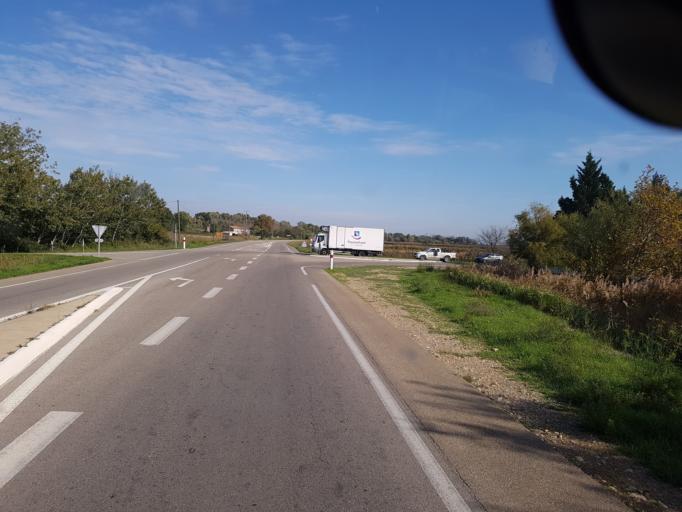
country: FR
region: Languedoc-Roussillon
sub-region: Departement du Gard
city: Saint-Gilles
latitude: 43.6651
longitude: 4.4660
